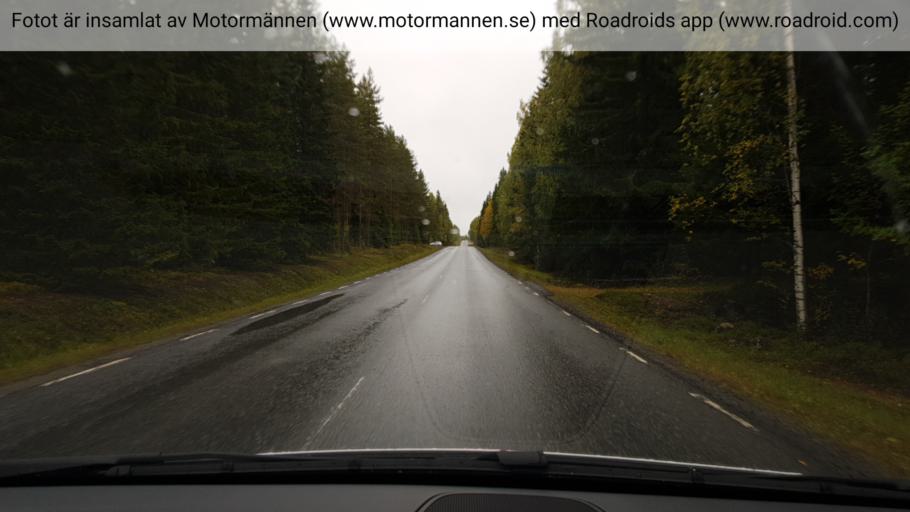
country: SE
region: Vaesterbotten
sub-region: Umea Kommun
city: Ersmark
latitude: 64.0048
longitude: 20.2443
